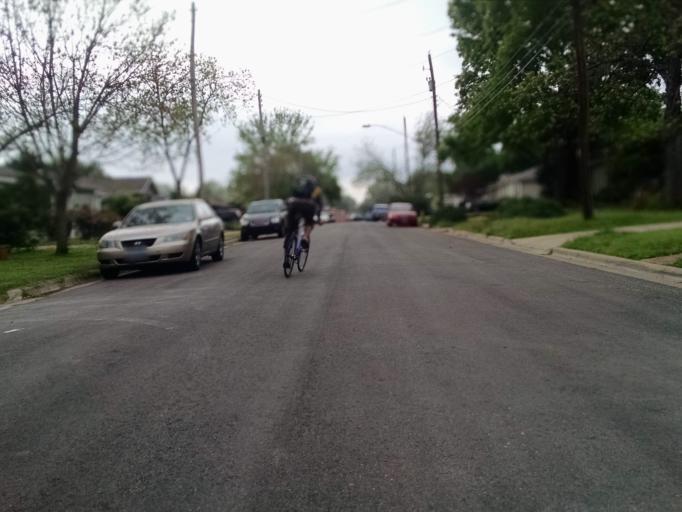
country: US
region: Texas
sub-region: Travis County
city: Austin
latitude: 30.3424
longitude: -97.7238
